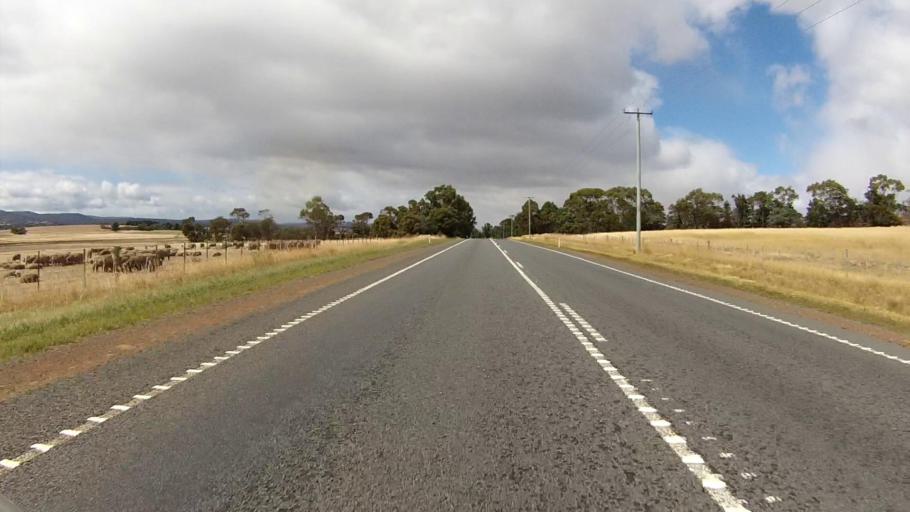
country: AU
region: Tasmania
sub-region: Northern Midlands
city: Evandale
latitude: -41.9804
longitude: 147.5051
